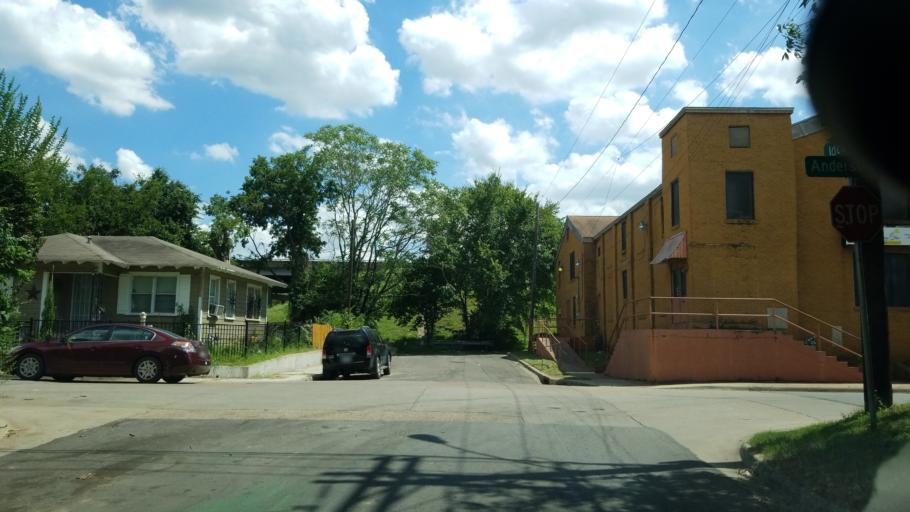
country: US
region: Texas
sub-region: Dallas County
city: Dallas
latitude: 32.7481
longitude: -96.7507
